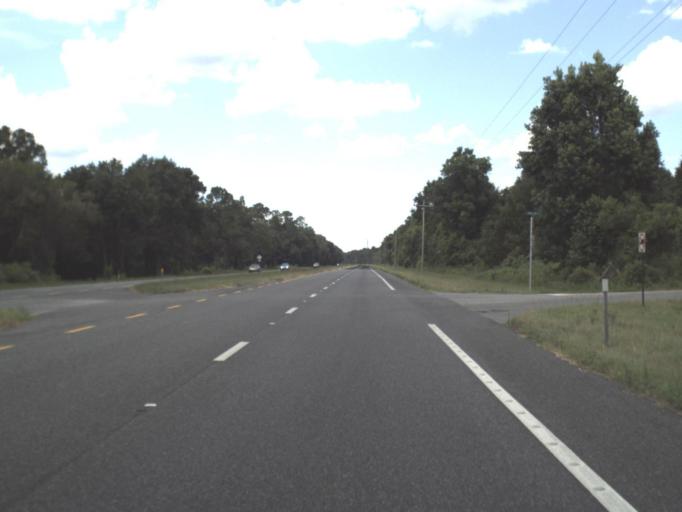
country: US
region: Florida
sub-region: Taylor County
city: Perry
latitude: 30.1798
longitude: -83.6374
